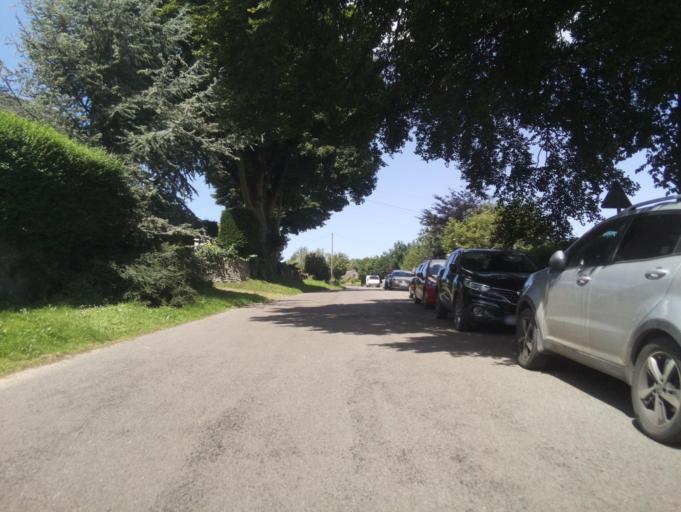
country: GB
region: England
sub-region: Derbyshire
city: Tideswell
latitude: 53.2368
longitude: -1.7915
